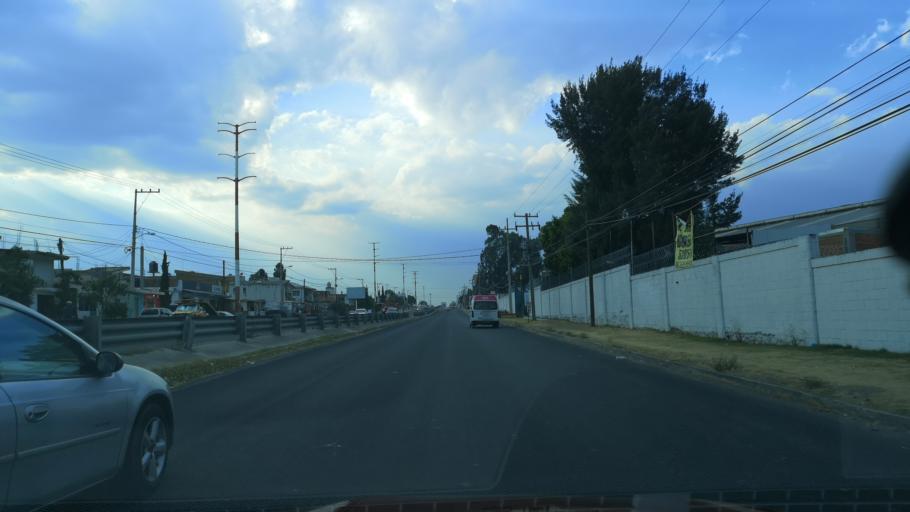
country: MX
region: Puebla
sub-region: Juan C. Bonilla
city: Santa Maria Zacatepec
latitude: 19.1100
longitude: -98.3536
